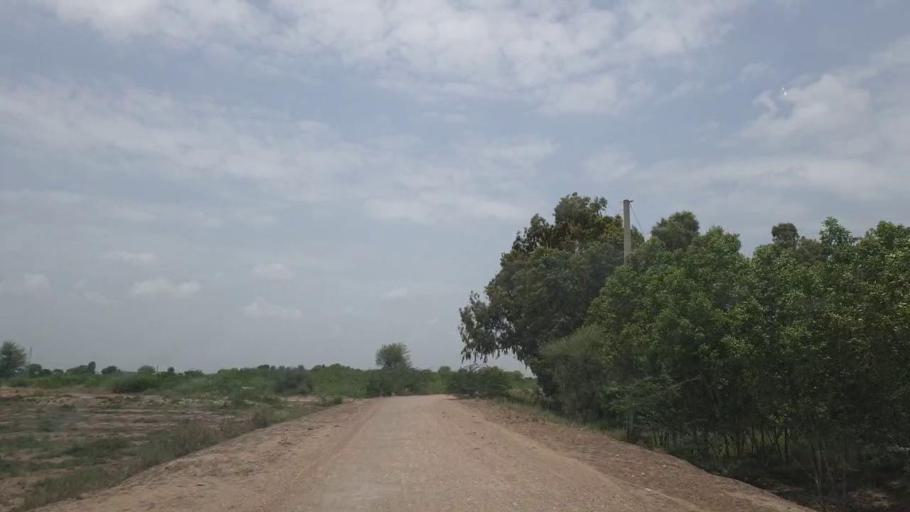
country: PK
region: Sindh
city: Naukot
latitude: 24.9285
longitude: 69.1986
